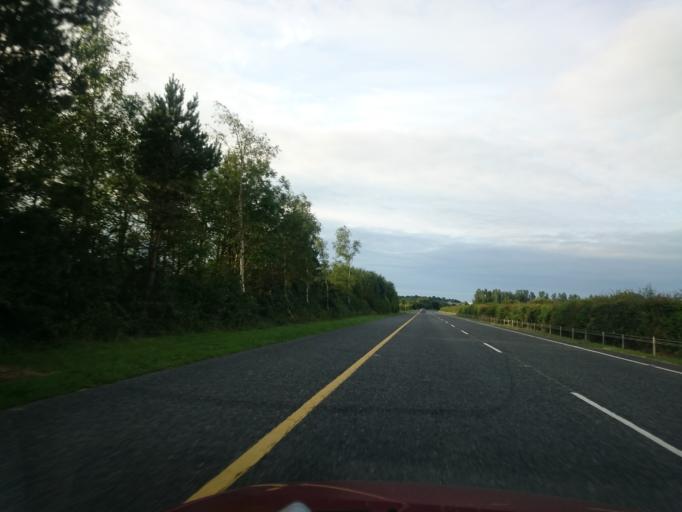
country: IE
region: Leinster
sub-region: Wicklow
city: Arklow
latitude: 52.7873
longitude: -6.1779
